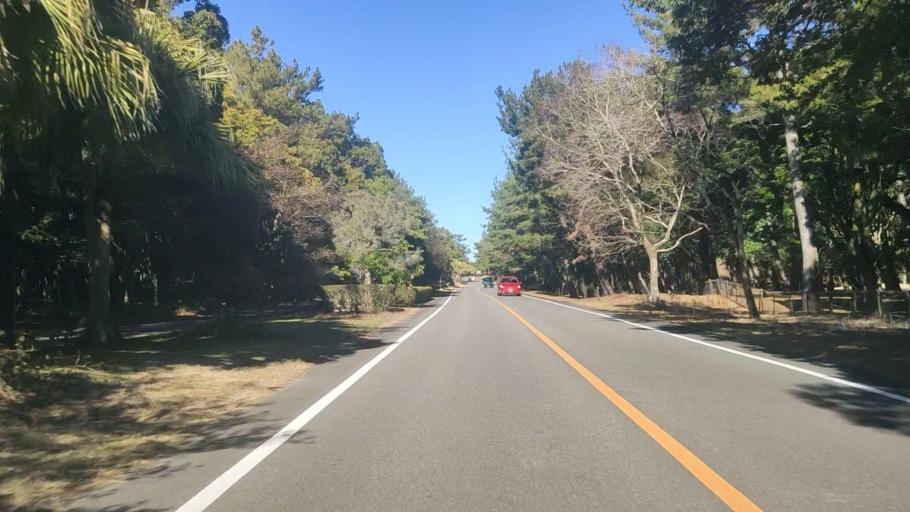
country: JP
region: Miyazaki
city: Miyazaki-shi
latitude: 31.9492
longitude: 131.4659
